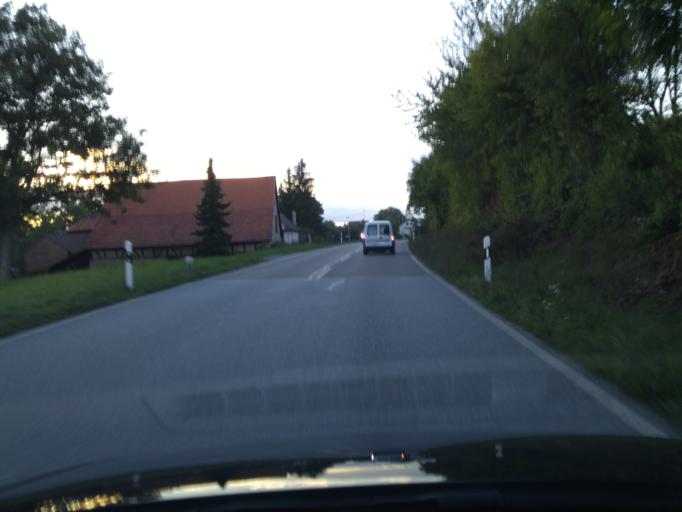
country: DE
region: Baden-Wuerttemberg
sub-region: Regierungsbezirk Stuttgart
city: Bad Rappenau
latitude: 49.2103
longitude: 9.1030
